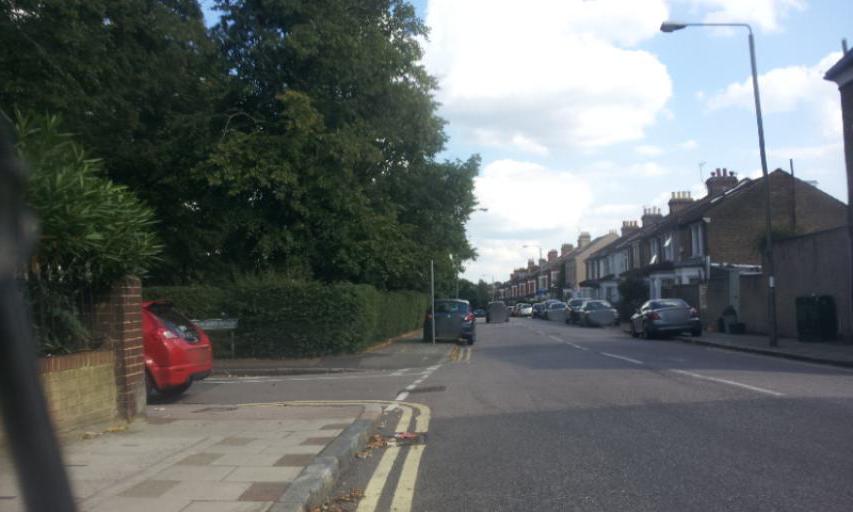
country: GB
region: England
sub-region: Greater London
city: Beckenham
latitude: 51.4192
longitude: -0.0517
